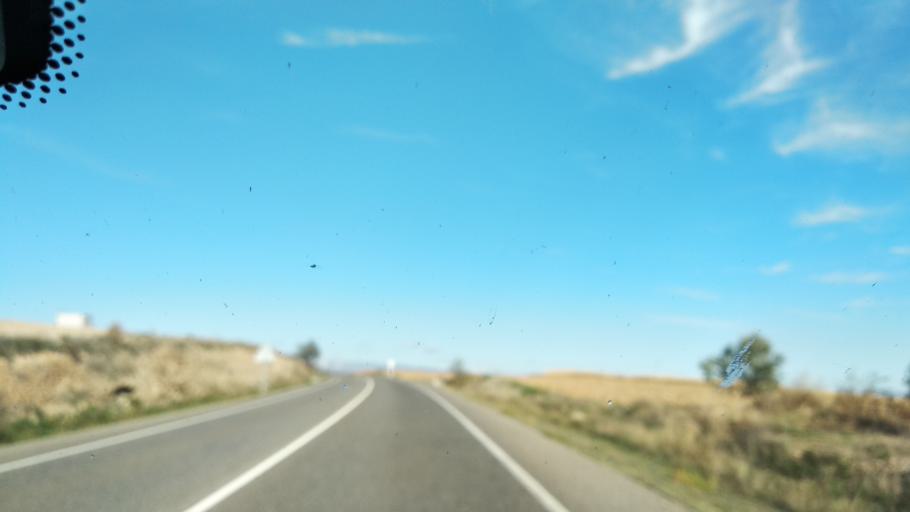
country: ES
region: Catalonia
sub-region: Provincia de Lleida
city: Termens
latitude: 41.7188
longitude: 0.7269
